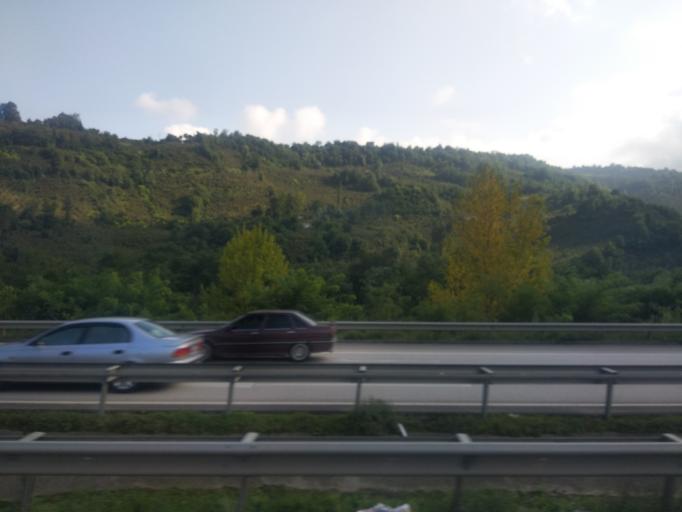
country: TR
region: Ordu
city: Ordu
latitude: 40.9888
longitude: 37.8039
